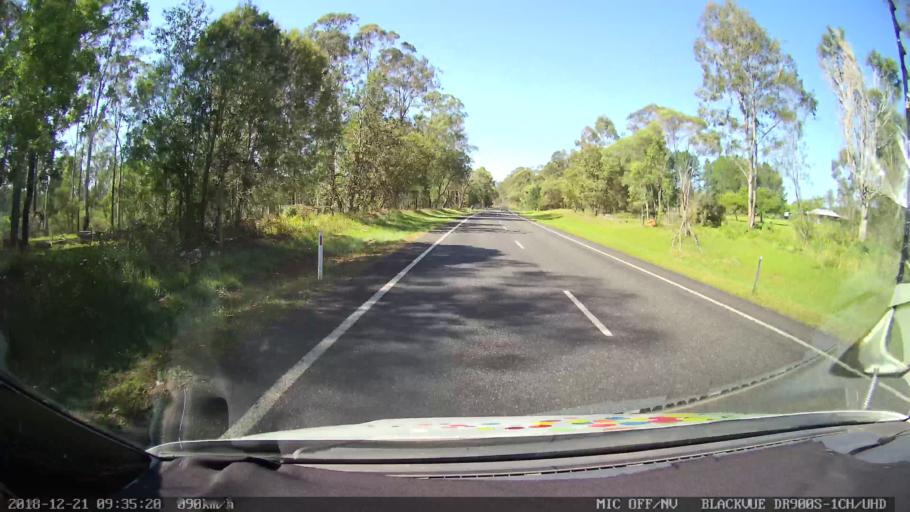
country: AU
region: New South Wales
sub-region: Clarence Valley
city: Grafton
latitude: -29.5094
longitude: 152.9817
